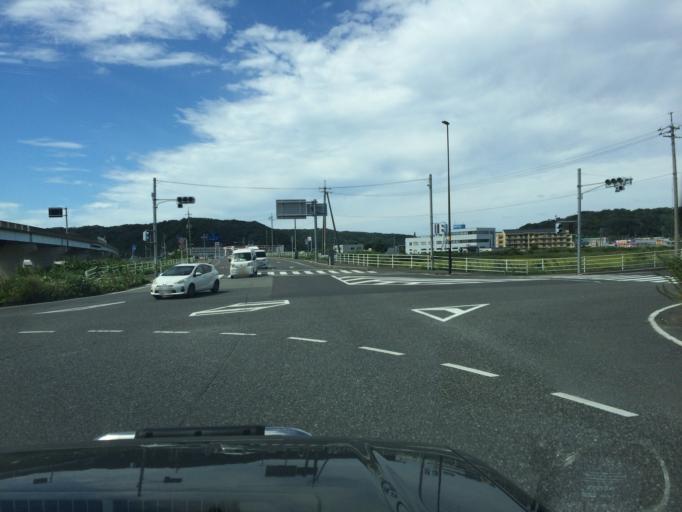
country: JP
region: Tottori
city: Kurayoshi
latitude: 35.5130
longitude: 134.0021
